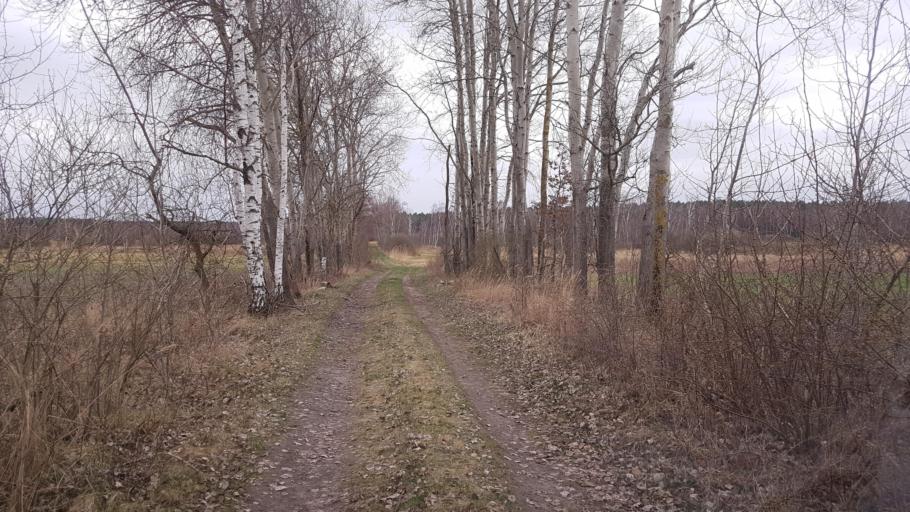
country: DE
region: Brandenburg
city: Hohenleipisch
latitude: 51.5320
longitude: 13.6043
